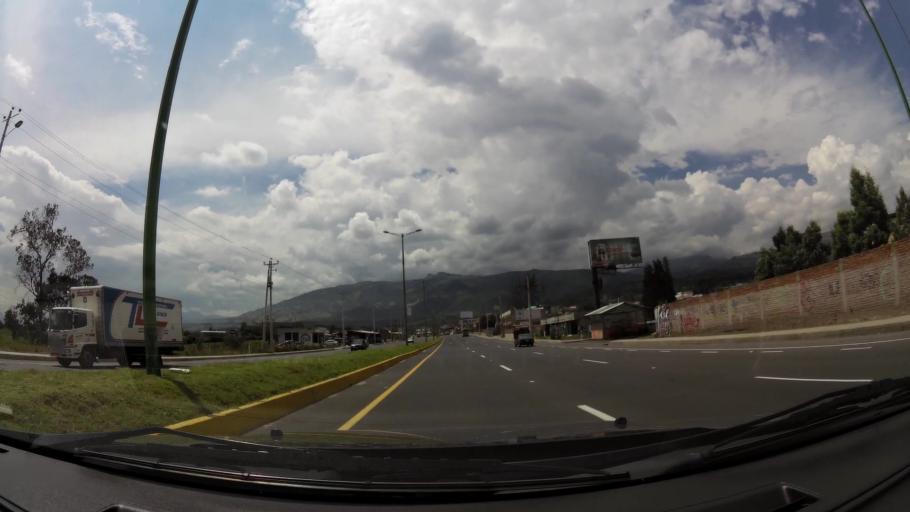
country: EC
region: Pichincha
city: Sangolqui
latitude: -0.2242
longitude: -78.3441
